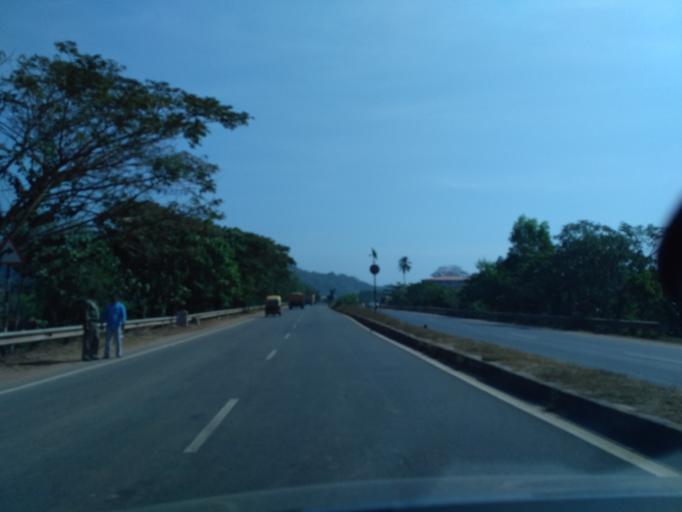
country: IN
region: Karnataka
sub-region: Dakshina Kannada
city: Ullal
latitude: 12.8673
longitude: 74.9133
